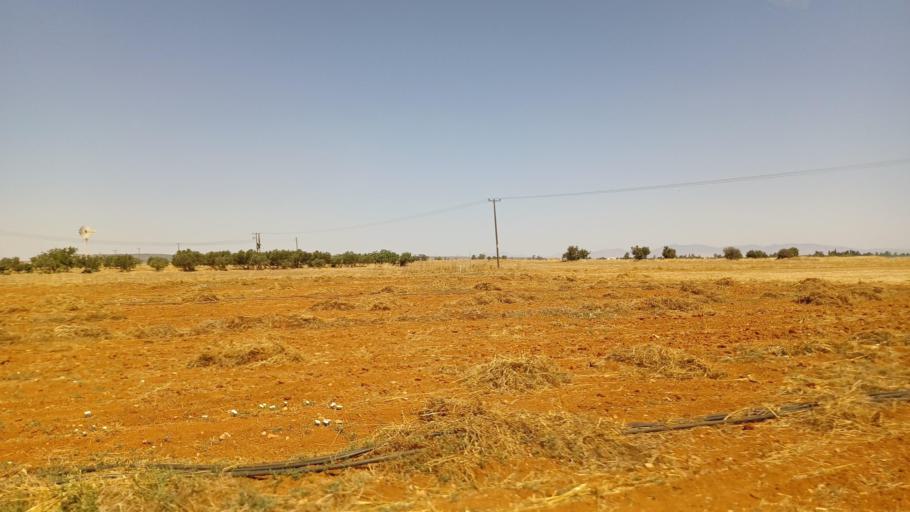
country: CY
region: Larnaka
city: Xylotymbou
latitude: 35.0255
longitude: 33.7283
